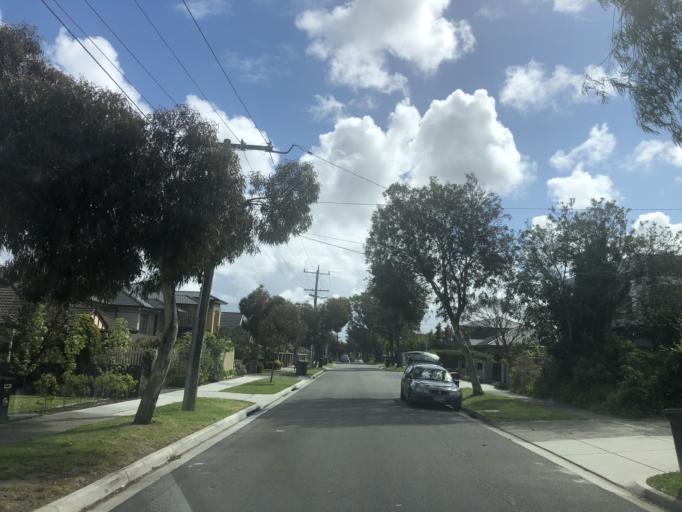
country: AU
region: Victoria
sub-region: Monash
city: Ashwood
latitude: -37.8766
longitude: 145.1178
